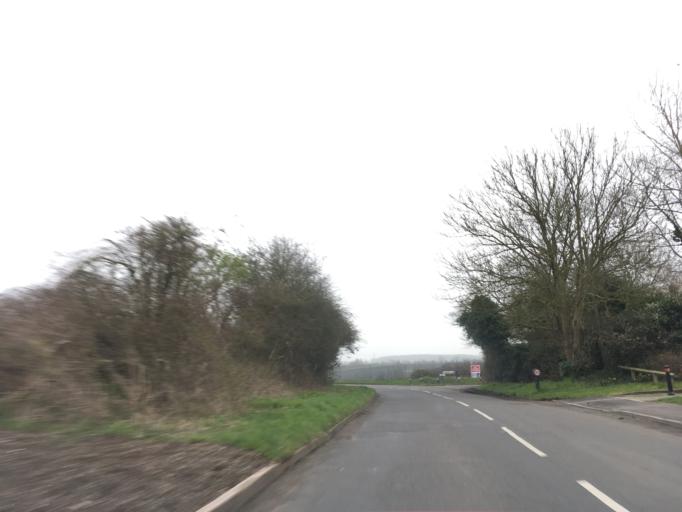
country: GB
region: England
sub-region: South Gloucestershire
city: Almondsbury
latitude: 51.5579
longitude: -2.5468
